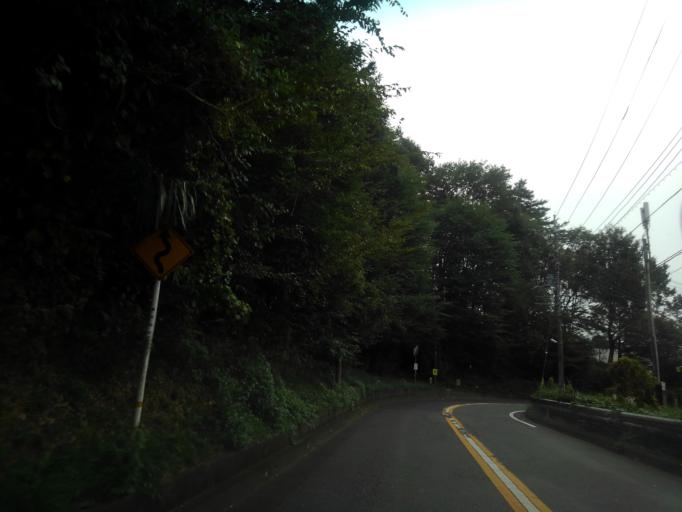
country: JP
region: Tokyo
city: Higashimurayama-shi
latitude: 35.7570
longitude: 139.4160
